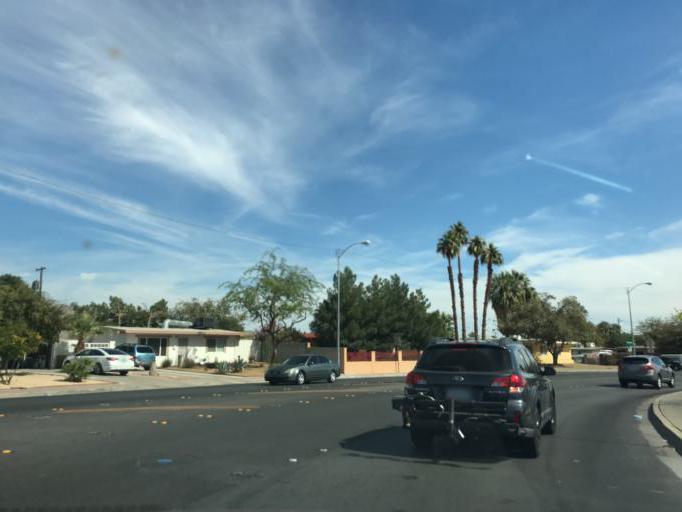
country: US
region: Nevada
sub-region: Clark County
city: Winchester
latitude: 36.1310
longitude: -115.0829
